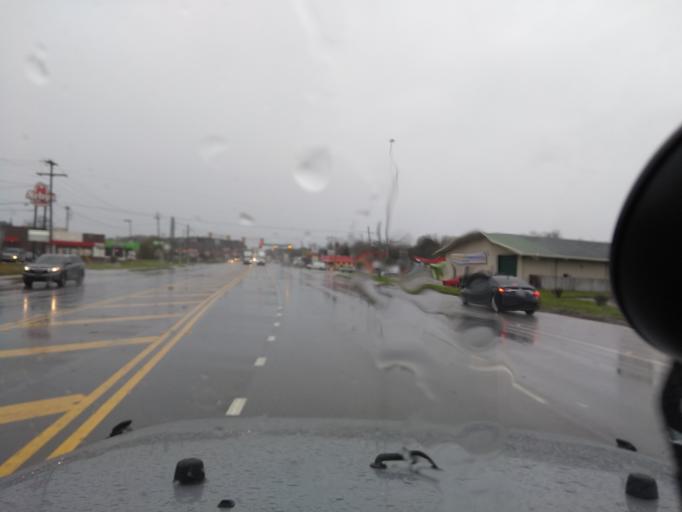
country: US
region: Georgia
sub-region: Chatham County
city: Garden City
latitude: 32.0975
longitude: -81.1419
